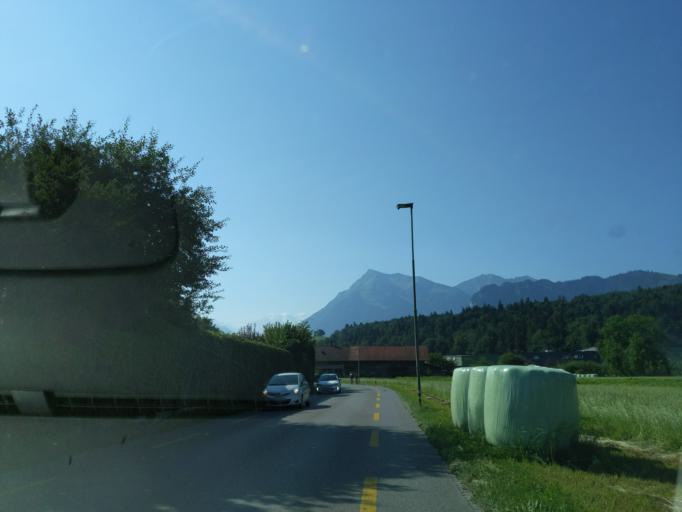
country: CH
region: Bern
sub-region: Thun District
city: Thun
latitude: 46.7282
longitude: 7.6149
